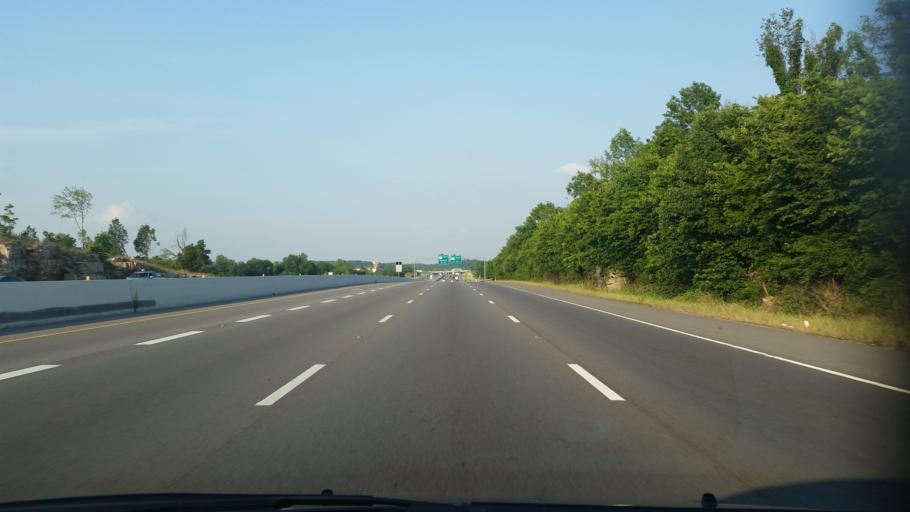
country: US
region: Tennessee
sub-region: Wilson County
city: Rural Hill
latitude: 36.1826
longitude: -86.4248
